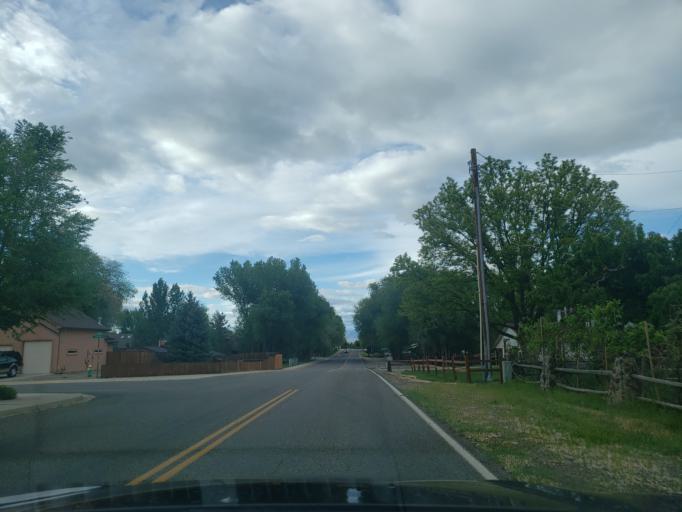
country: US
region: Colorado
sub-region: Mesa County
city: Redlands
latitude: 39.0999
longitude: -108.6687
